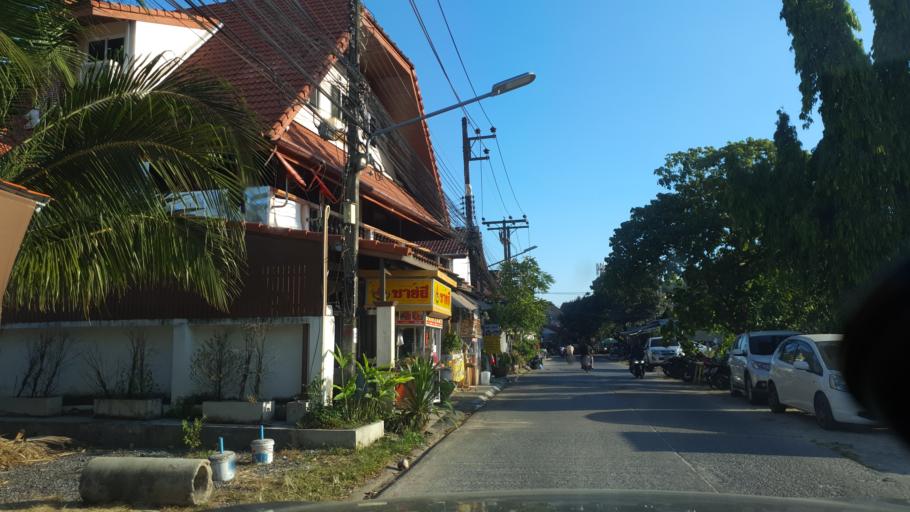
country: TH
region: Phuket
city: Kathu
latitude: 7.9037
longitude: 98.3300
